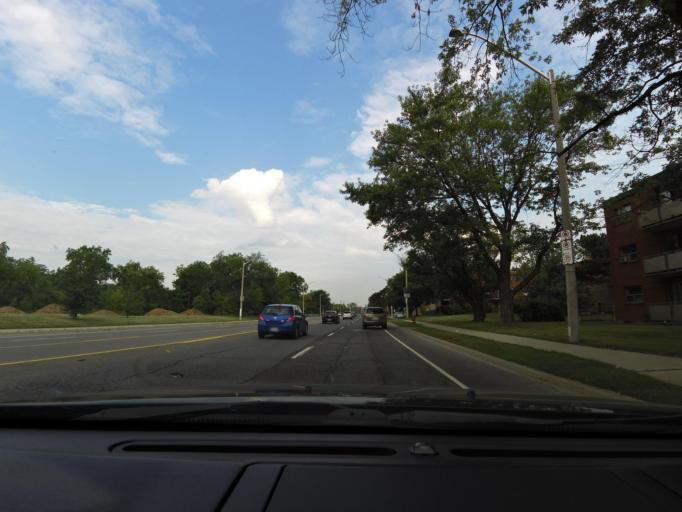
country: CA
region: Ontario
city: Hamilton
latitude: 43.2214
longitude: -79.7781
